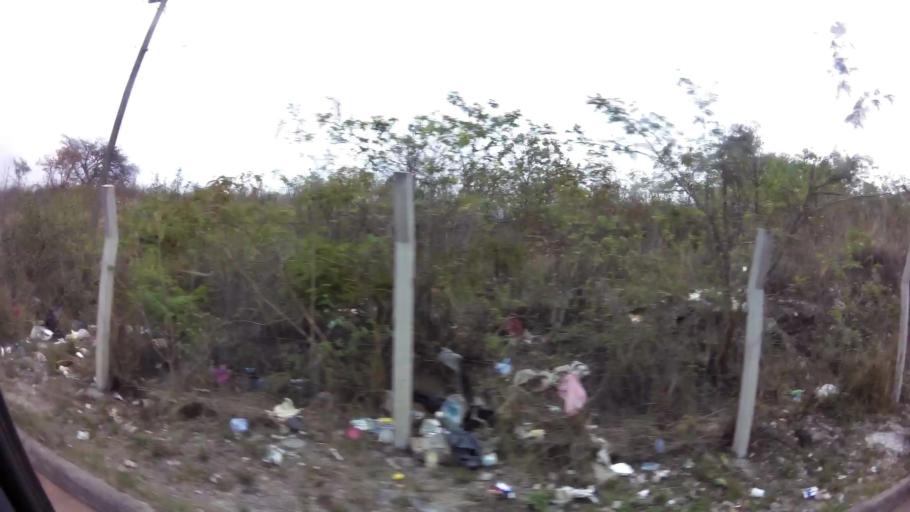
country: HN
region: Francisco Morazan
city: Tegucigalpa
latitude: 14.0689
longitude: -87.2415
